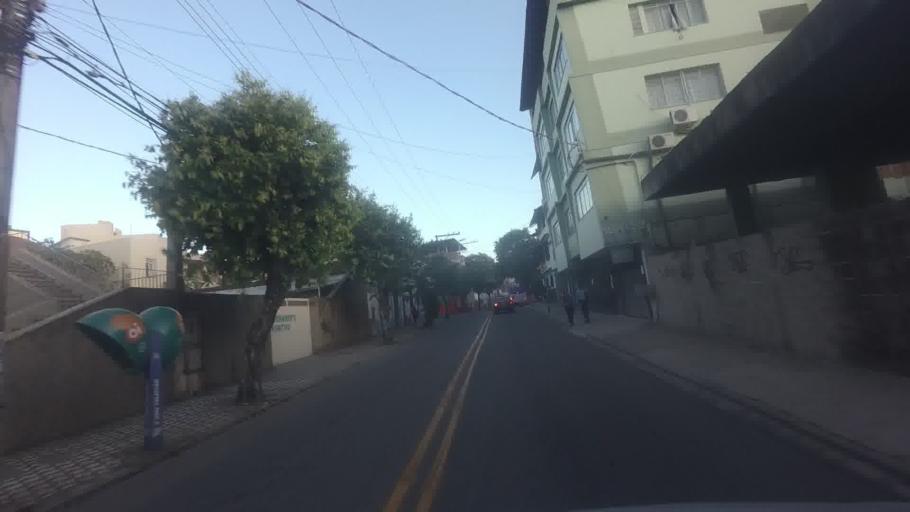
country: BR
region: Espirito Santo
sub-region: Cachoeiro De Itapemirim
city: Cachoeiro de Itapemirim
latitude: -20.8505
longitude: -41.1091
